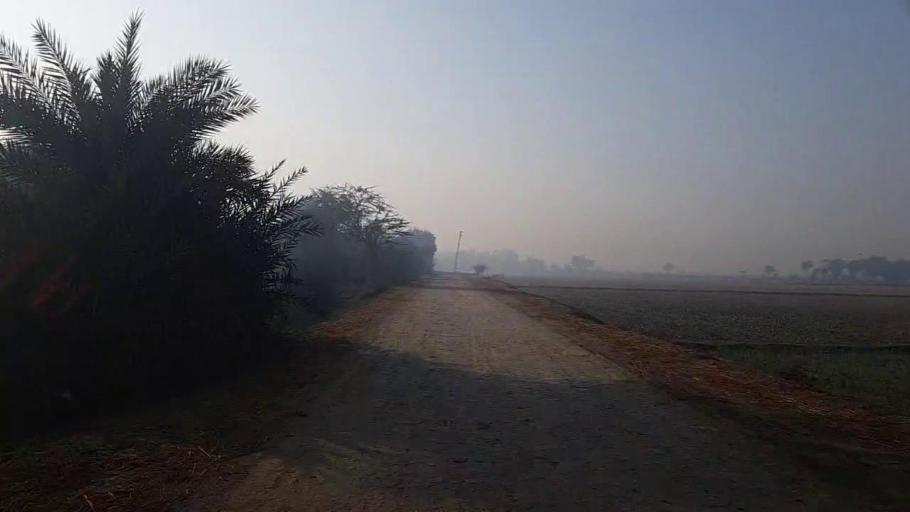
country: PK
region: Sindh
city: Mehar
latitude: 27.1373
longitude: 67.8232
